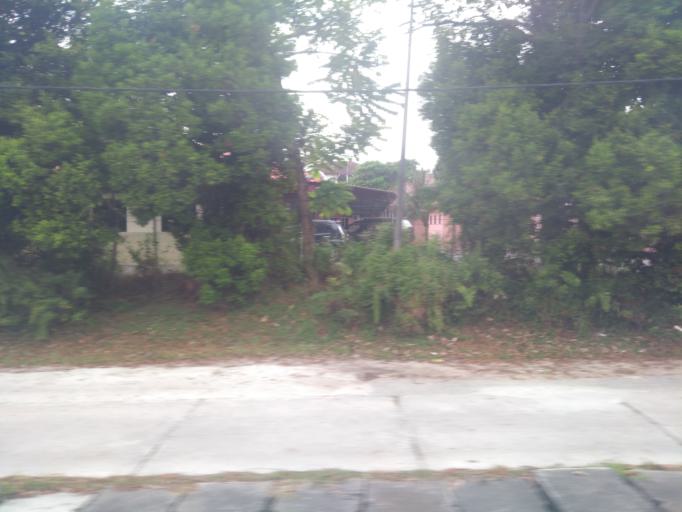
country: MY
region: Johor
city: Johor Bahru
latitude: 1.4929
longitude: 103.7064
